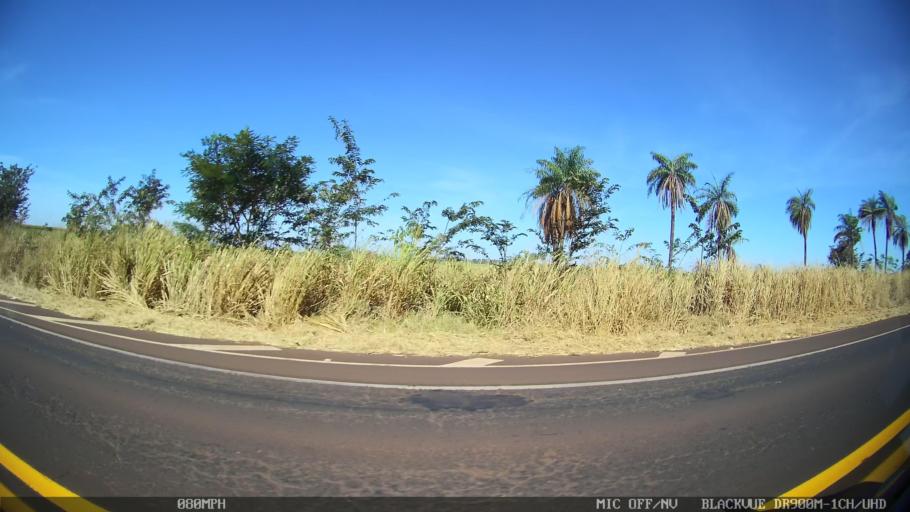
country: BR
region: Sao Paulo
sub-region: Barretos
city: Barretos
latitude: -20.4676
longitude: -48.4793
